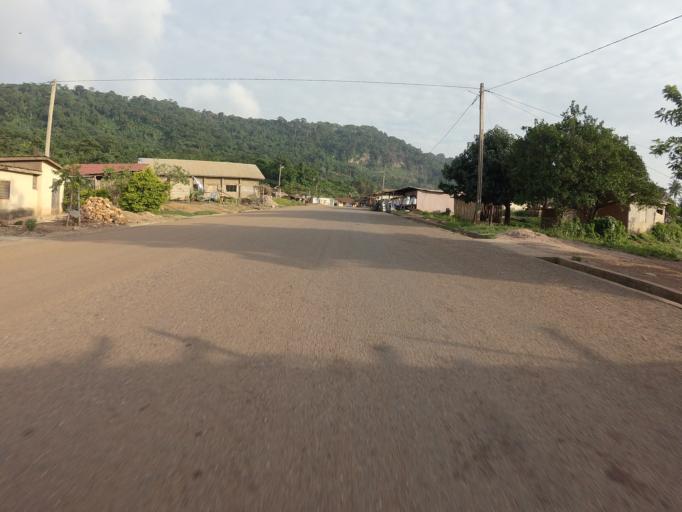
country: TG
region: Plateaux
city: Kpalime
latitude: 6.9210
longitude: 0.4611
